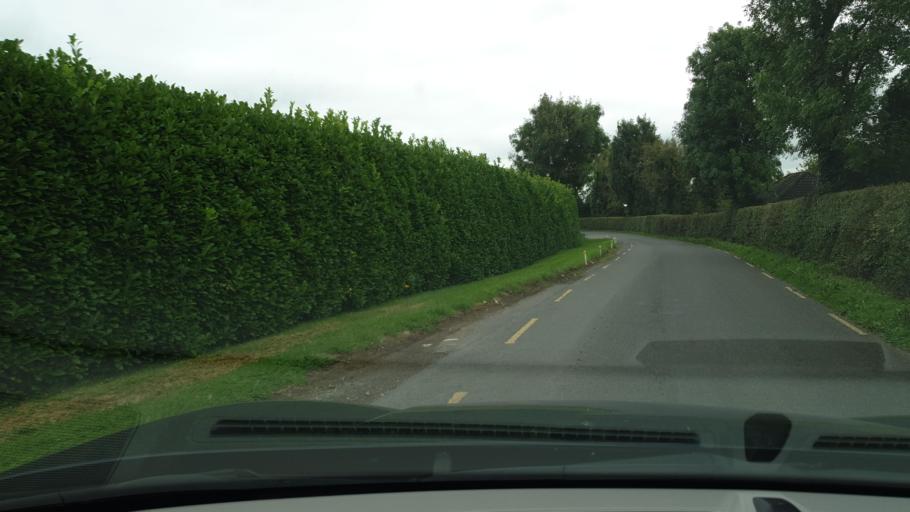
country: IE
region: Leinster
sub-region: Kildare
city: Clane
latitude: 53.3006
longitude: -6.7130
